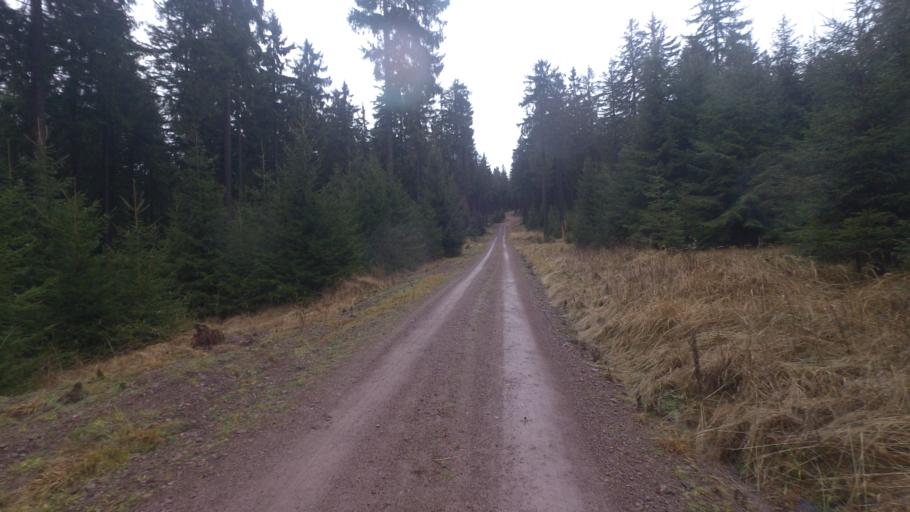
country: DE
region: Thuringia
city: Oberhof
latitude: 50.7149
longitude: 10.7558
